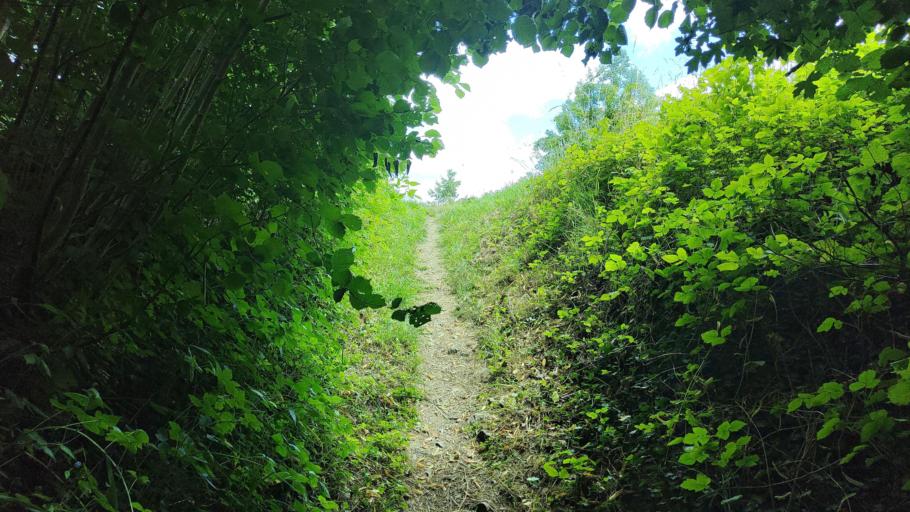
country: BE
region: Wallonia
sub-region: Province du Hainaut
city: Chimay
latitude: 50.0617
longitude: 4.3773
